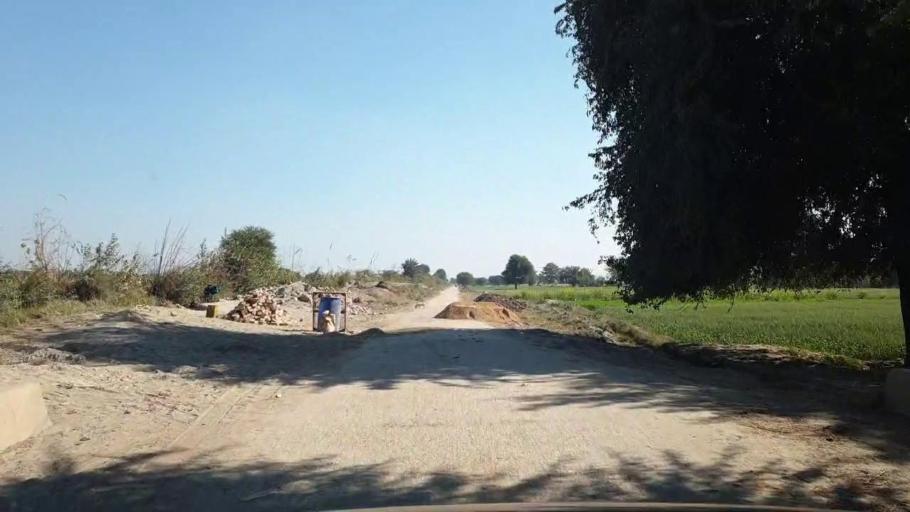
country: PK
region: Sindh
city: Shahpur Chakar
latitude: 26.1467
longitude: 68.6451
